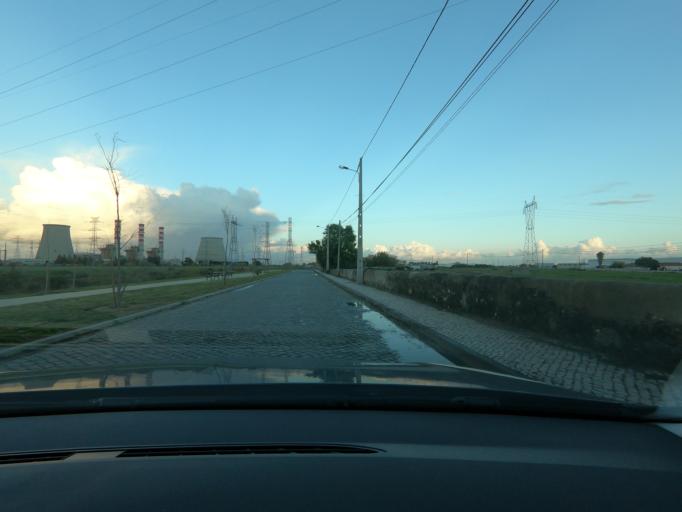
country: PT
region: Lisbon
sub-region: Alenquer
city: Carregado
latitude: 39.0110
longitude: -8.9604
